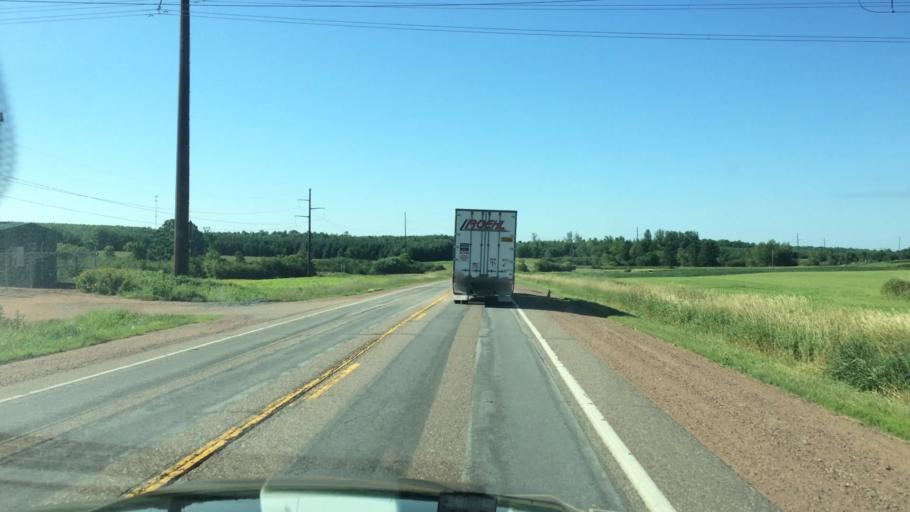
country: US
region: Wisconsin
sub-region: Marathon County
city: Athens
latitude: 44.9349
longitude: -90.0790
